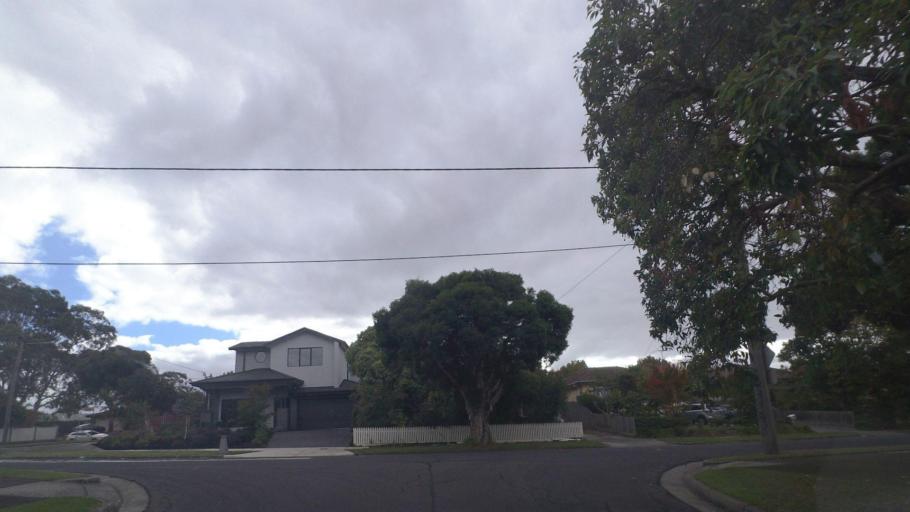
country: AU
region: Victoria
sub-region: Whitehorse
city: Forest Hill
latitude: -37.8327
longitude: 145.1679
